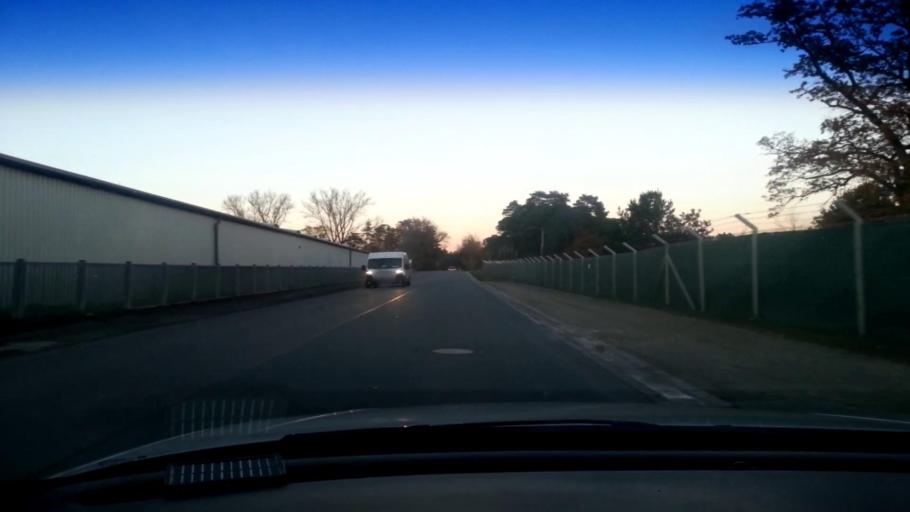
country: DE
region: Bavaria
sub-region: Upper Franconia
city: Bamberg
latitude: 49.8909
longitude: 10.9269
